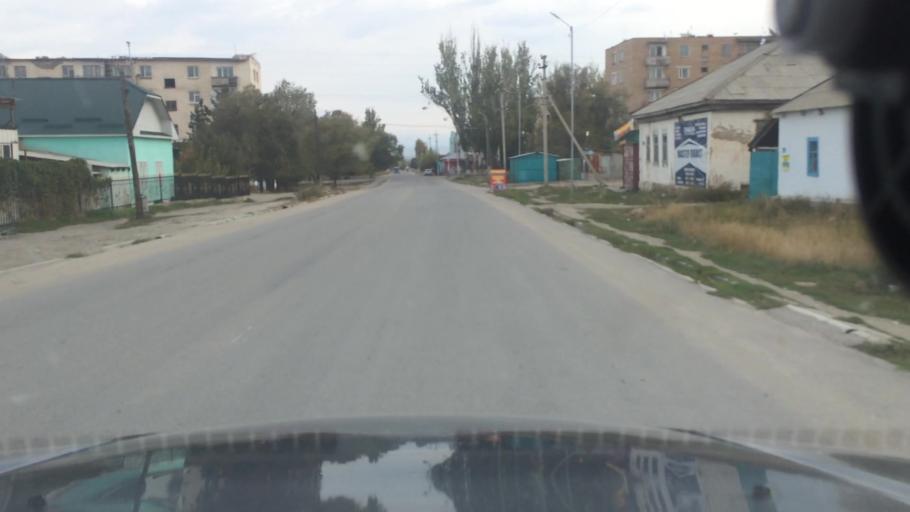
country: KG
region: Ysyk-Koel
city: Karakol
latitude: 42.4949
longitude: 78.3903
